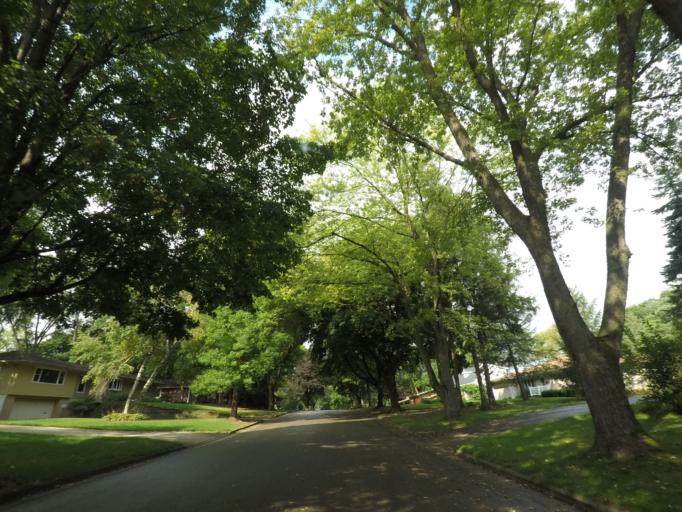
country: US
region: Wisconsin
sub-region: Dane County
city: Shorewood Hills
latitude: 43.0359
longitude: -89.4687
